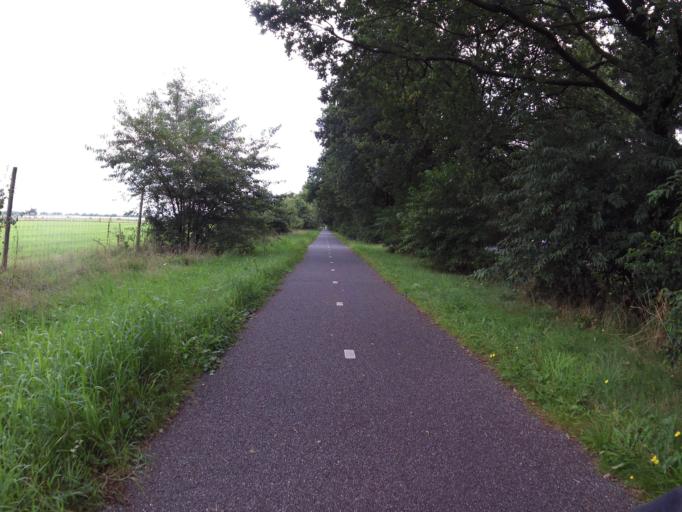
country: NL
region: Drenthe
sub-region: Gemeente Borger-Odoorn
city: Borger
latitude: 52.9316
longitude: 6.7594
